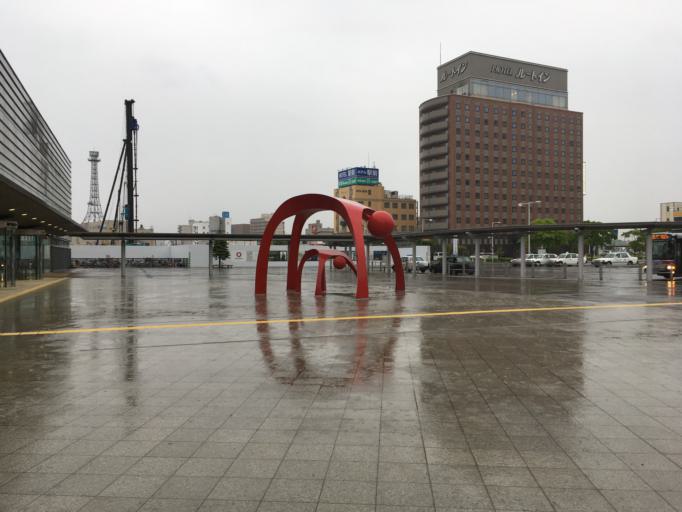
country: JP
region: Hokkaido
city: Hakodate
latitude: 41.7736
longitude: 140.7266
